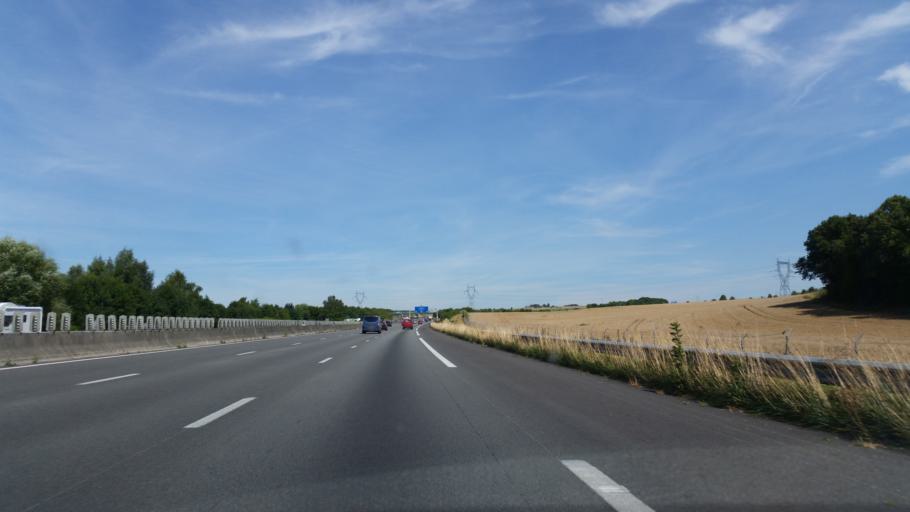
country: FR
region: Picardie
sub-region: Departement de la Somme
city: Peronne
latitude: 49.9627
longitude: 2.8570
